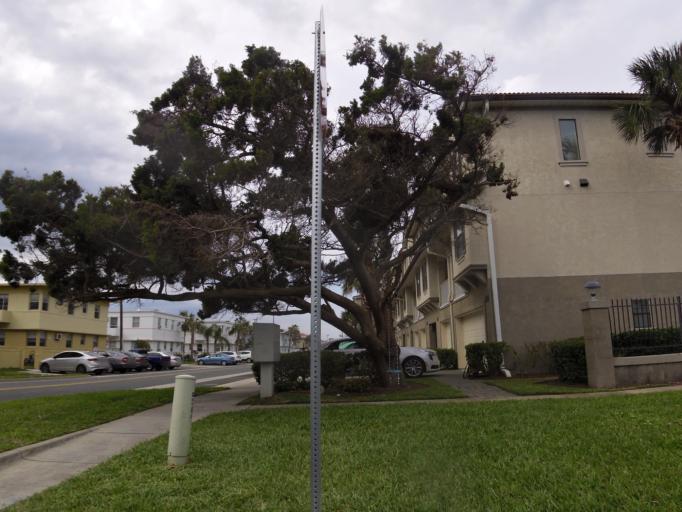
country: US
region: Florida
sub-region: Duval County
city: Jacksonville Beach
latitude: 30.2968
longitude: -81.3923
